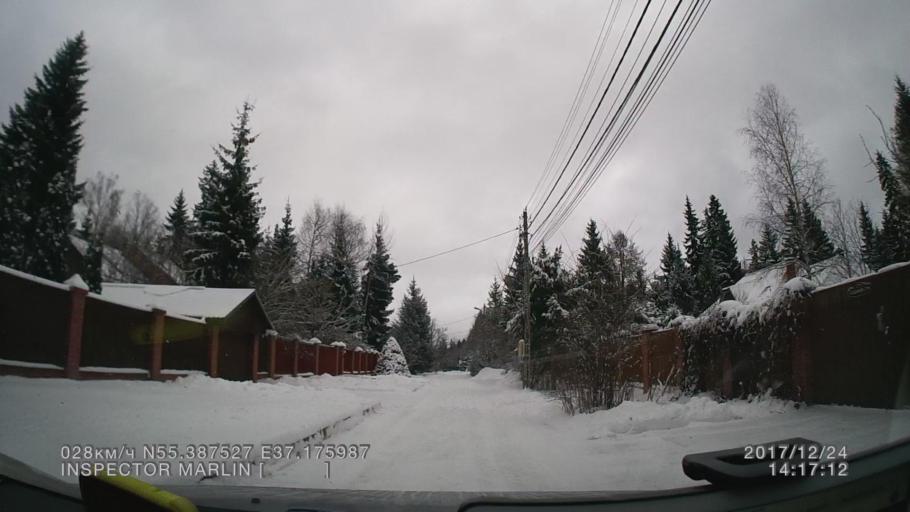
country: RU
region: Moskovskaya
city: Troitsk
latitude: 55.3875
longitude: 37.1761
